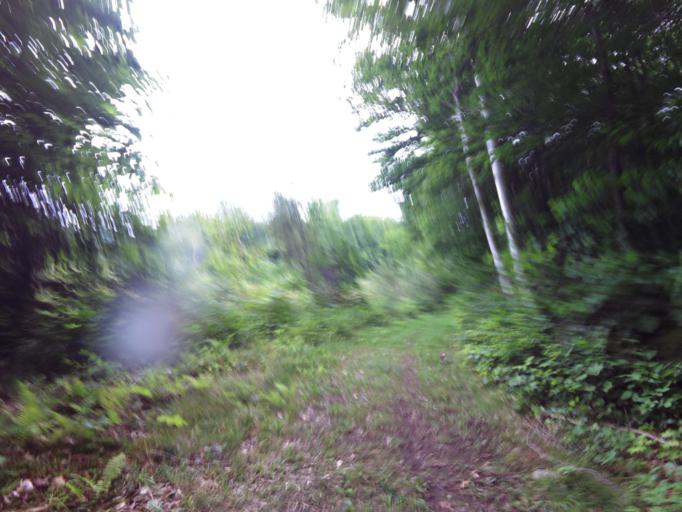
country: CA
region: Quebec
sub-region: Outaouais
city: Wakefield
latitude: 45.6084
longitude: -76.0486
